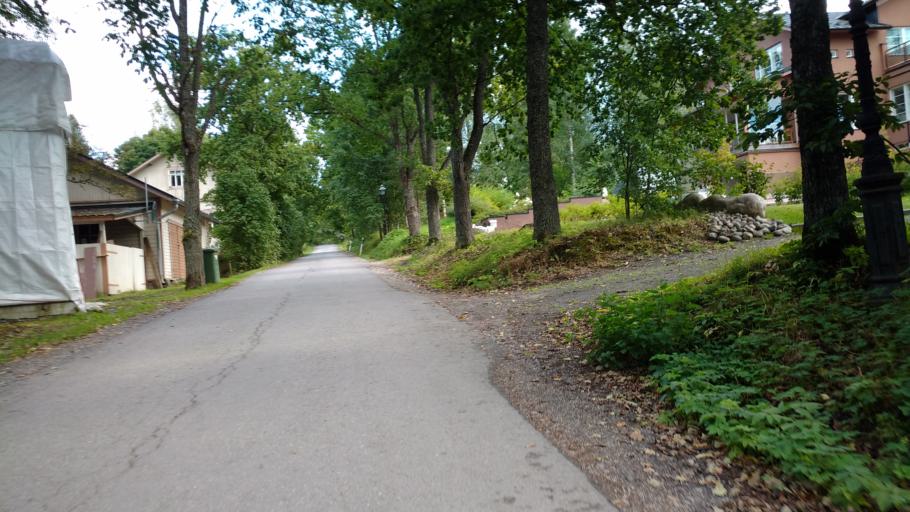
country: FI
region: Varsinais-Suomi
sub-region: Salo
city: Saerkisalo
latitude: 60.2187
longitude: 22.9029
